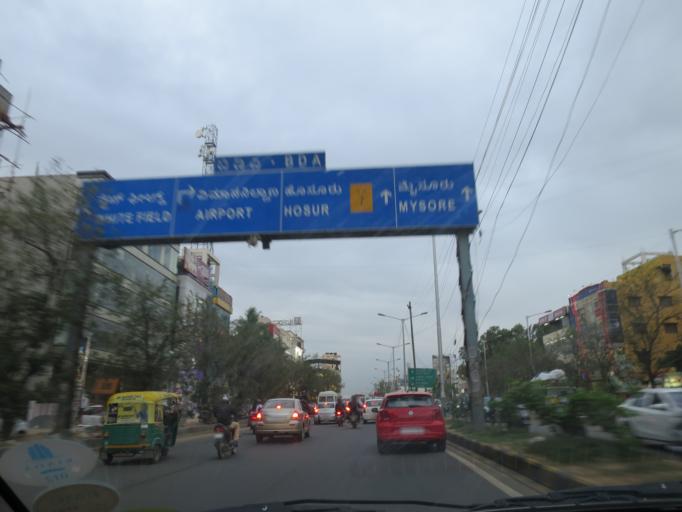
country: IN
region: Karnataka
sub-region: Bangalore Urban
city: Bangalore
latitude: 12.9610
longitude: 77.7015
